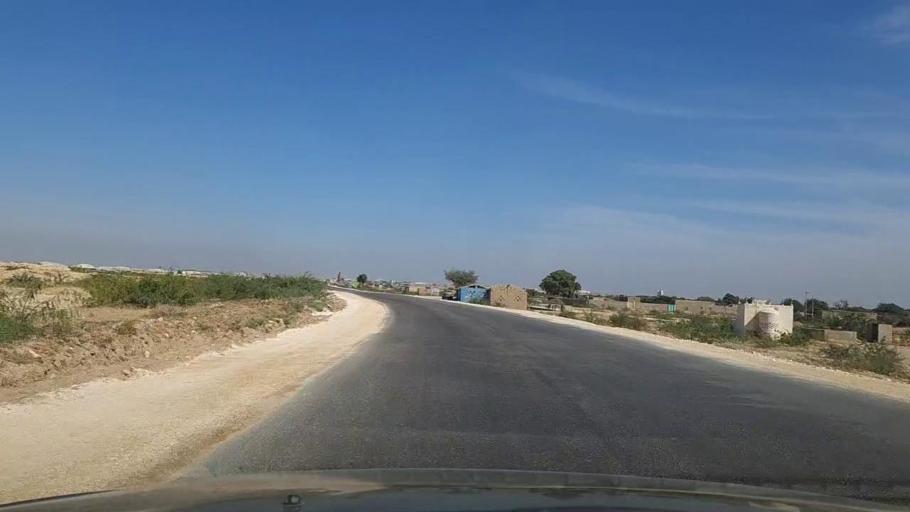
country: PK
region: Sindh
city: Kotri
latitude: 25.3191
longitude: 68.2292
